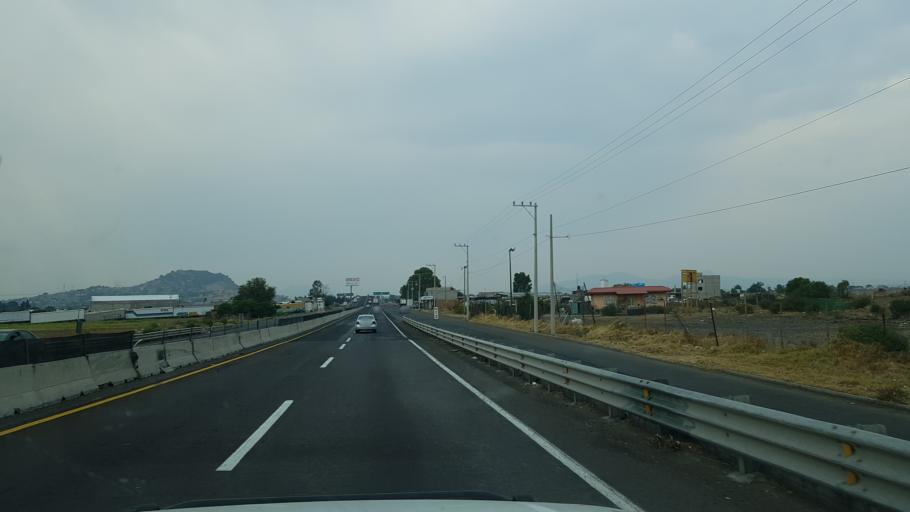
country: MX
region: Mexico
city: Miraflores
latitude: 19.2257
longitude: -98.8367
